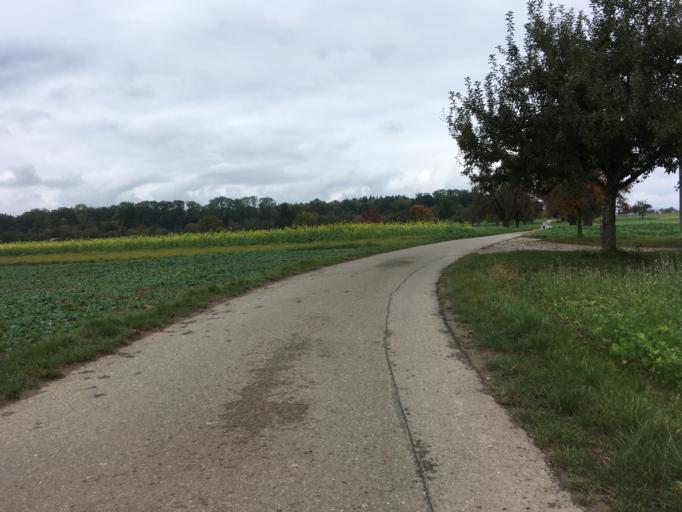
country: DE
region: Baden-Wuerttemberg
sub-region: Tuebingen Region
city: Gomaringen
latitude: 48.4857
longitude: 9.0953
